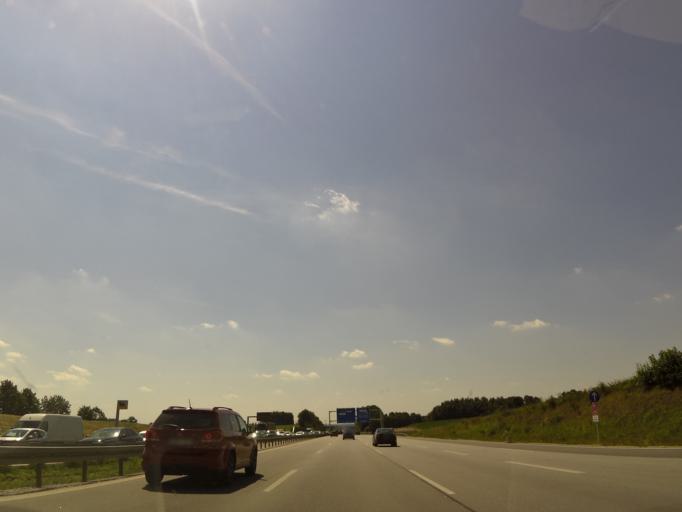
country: DE
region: Bavaria
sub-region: Upper Bavaria
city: Eching
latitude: 48.3346
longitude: 11.6106
